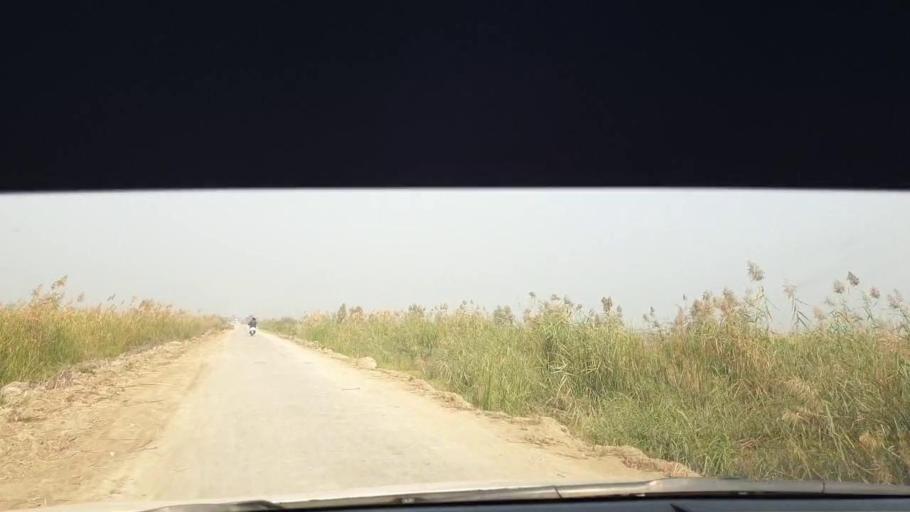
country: PK
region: Sindh
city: Berani
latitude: 25.7928
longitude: 68.8368
